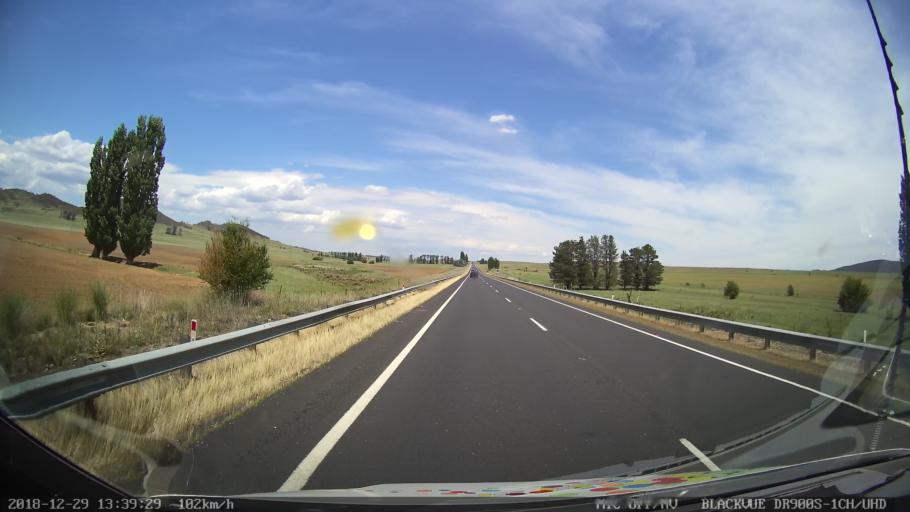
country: AU
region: New South Wales
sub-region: Cooma-Monaro
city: Cooma
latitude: -36.0136
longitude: 149.1472
